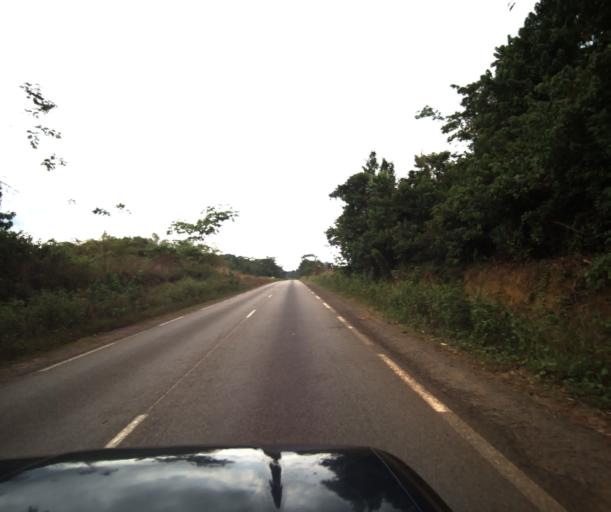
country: CM
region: Littoral
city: Edea
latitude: 3.8160
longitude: 10.3449
